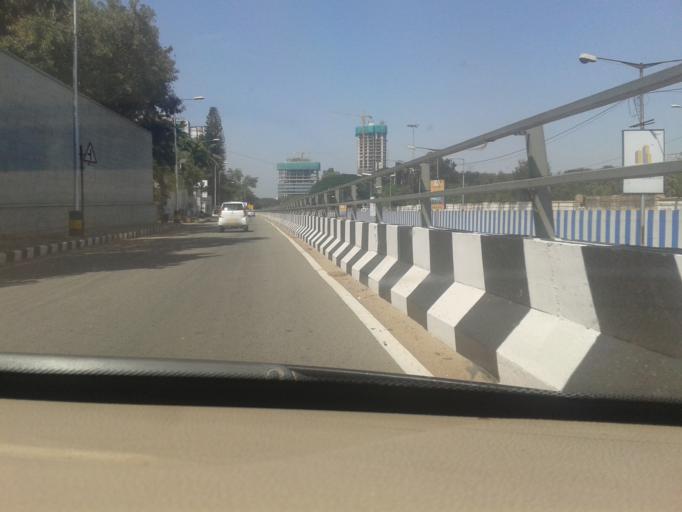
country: IN
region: Karnataka
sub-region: Bangalore Urban
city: Bangalore
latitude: 13.0123
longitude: 77.5838
